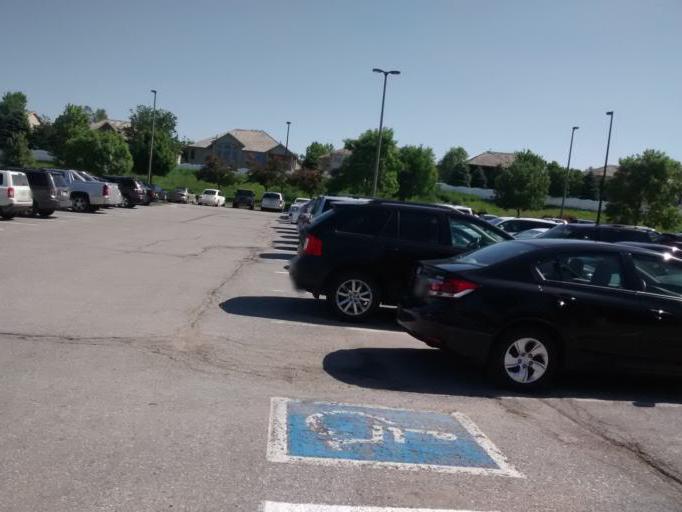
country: US
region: Nebraska
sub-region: Douglas County
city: Elkhorn
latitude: 41.2602
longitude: -96.1825
